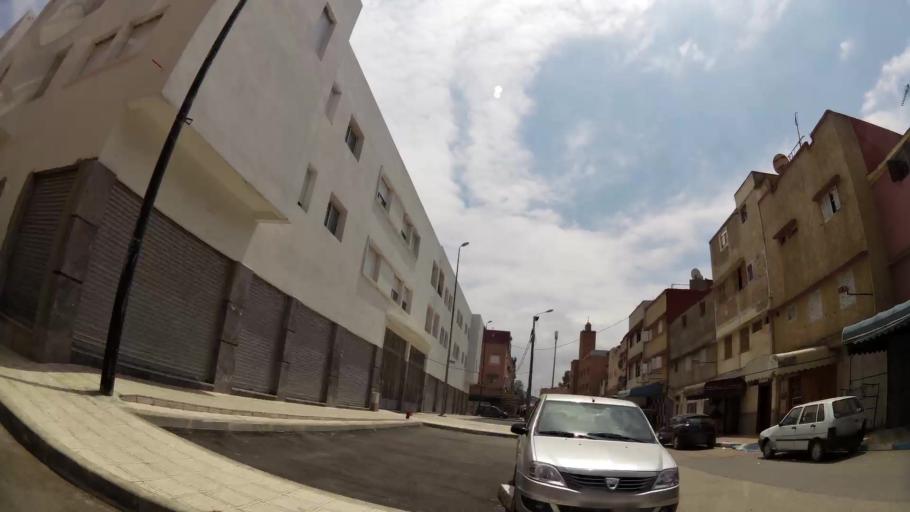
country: MA
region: Rabat-Sale-Zemmour-Zaer
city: Sale
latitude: 34.0520
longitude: -6.7876
